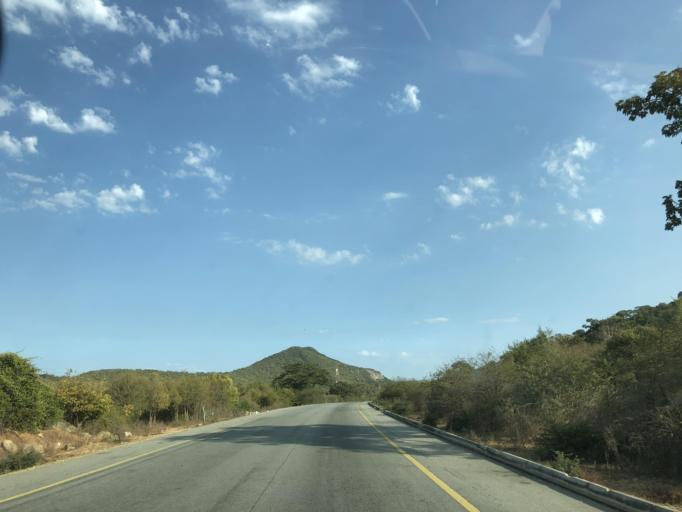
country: AO
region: Benguela
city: Benguela
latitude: -13.2663
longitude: 13.7926
